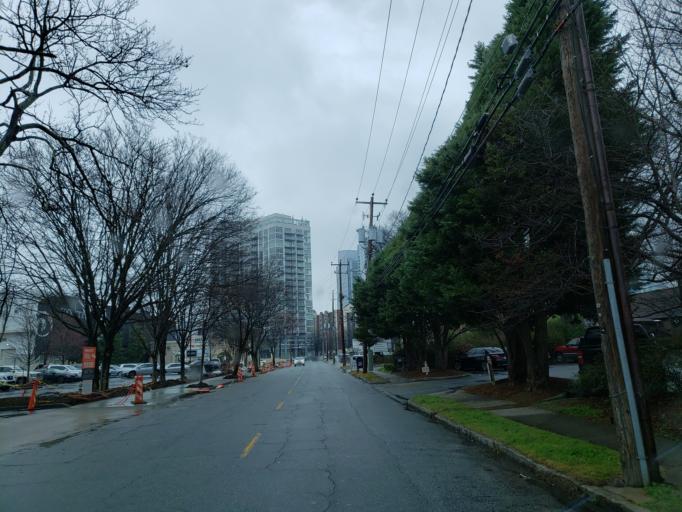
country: US
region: Georgia
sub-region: DeKalb County
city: North Atlanta
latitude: 33.8411
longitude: -84.3723
